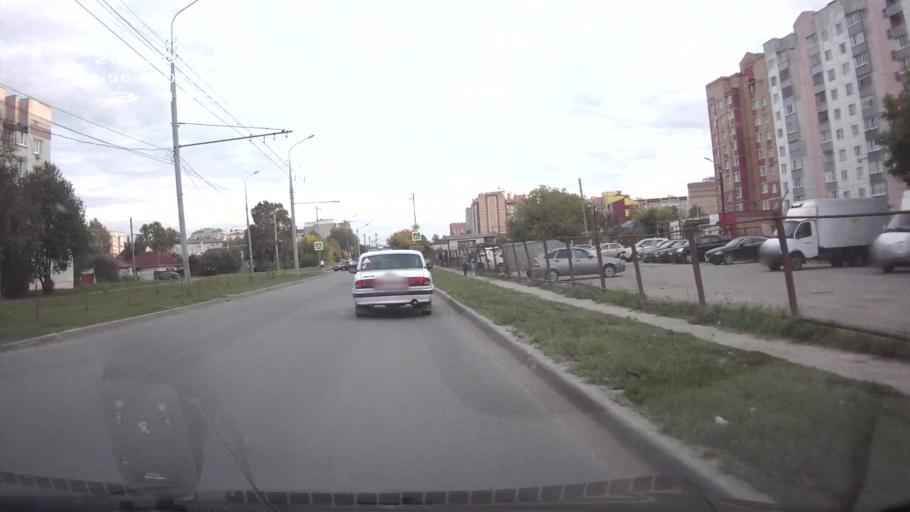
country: RU
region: Mariy-El
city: Yoshkar-Ola
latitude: 56.6497
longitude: 47.8553
